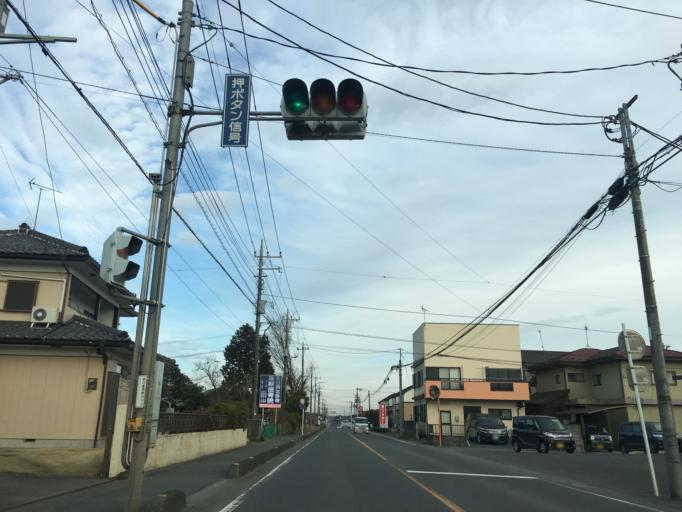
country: JP
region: Saitama
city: Hanno
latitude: 35.8978
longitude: 139.3589
